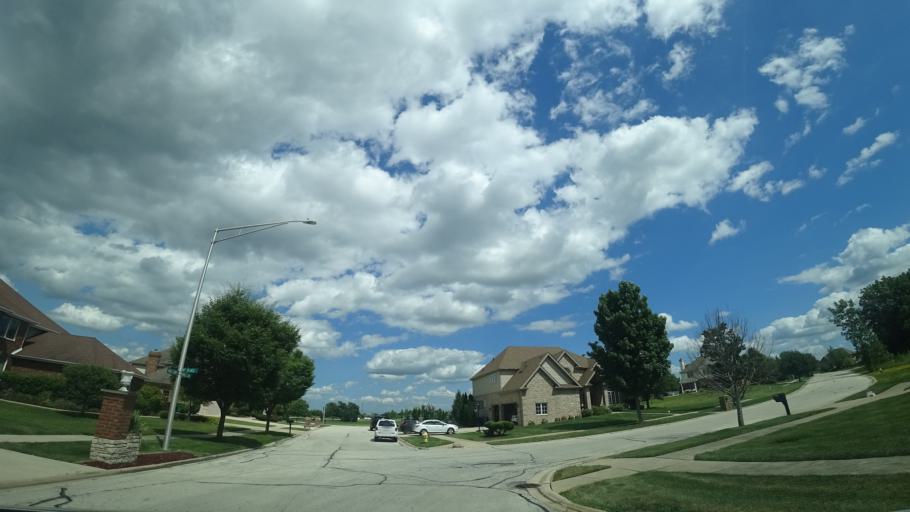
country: US
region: Illinois
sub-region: Will County
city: Homer Glen
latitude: 41.5910
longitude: -87.9082
